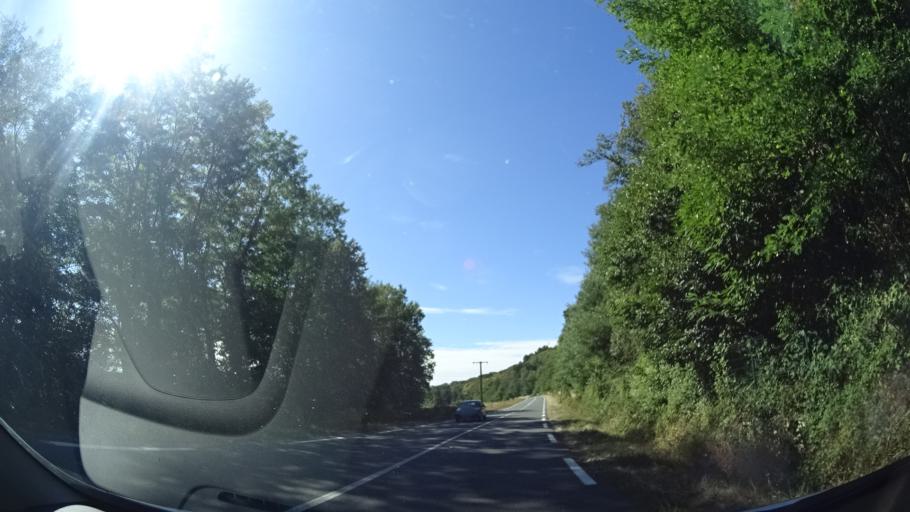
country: FR
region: Centre
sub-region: Departement du Loiret
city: Douchy
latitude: 47.9456
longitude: 3.0346
